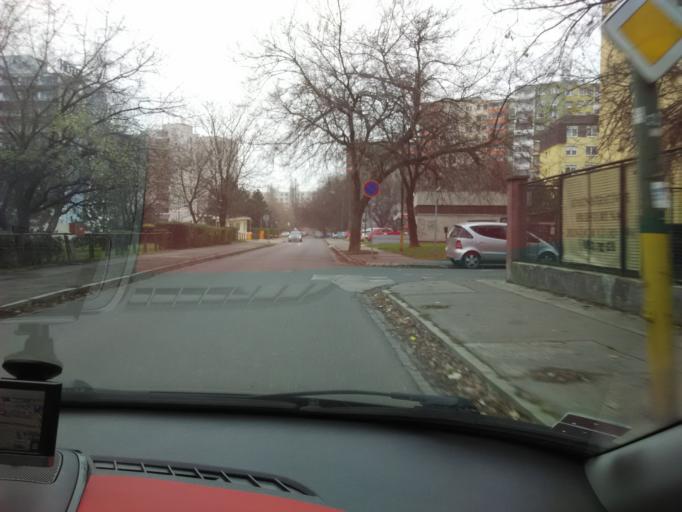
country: SK
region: Bratislavsky
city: Bratislava
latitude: 48.1589
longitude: 17.1411
